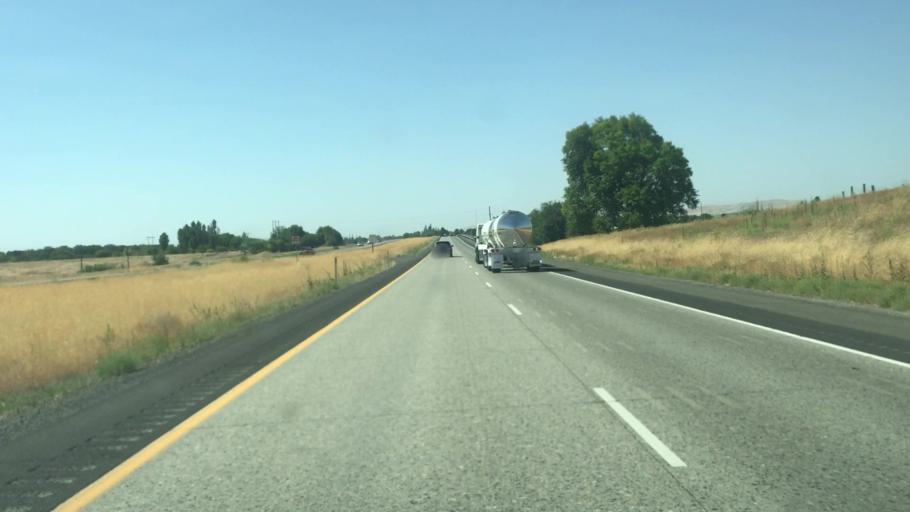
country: US
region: Washington
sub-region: Yakima County
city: Granger
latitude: 46.3699
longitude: -120.2136
